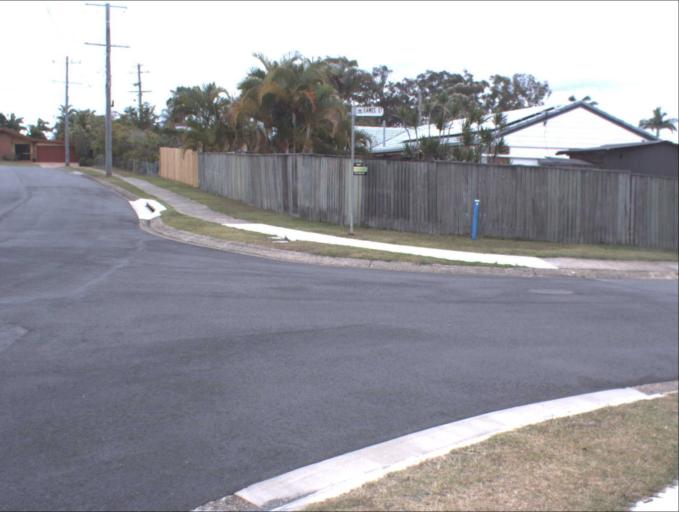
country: AU
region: Queensland
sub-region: Logan
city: Springwood
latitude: -27.6282
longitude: 153.1411
